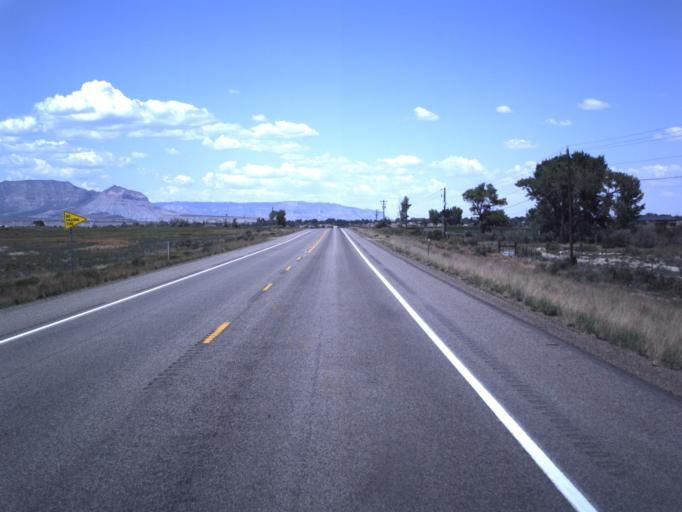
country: US
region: Utah
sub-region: Emery County
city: Castle Dale
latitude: 39.1949
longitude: -111.0241
